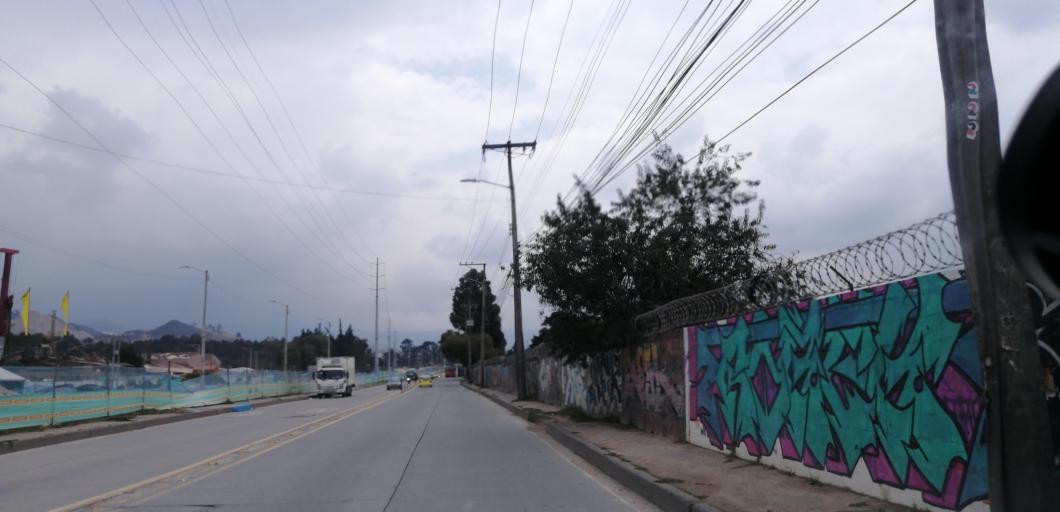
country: CO
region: Bogota D.C.
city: Bogota
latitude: 4.5421
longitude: -74.1207
